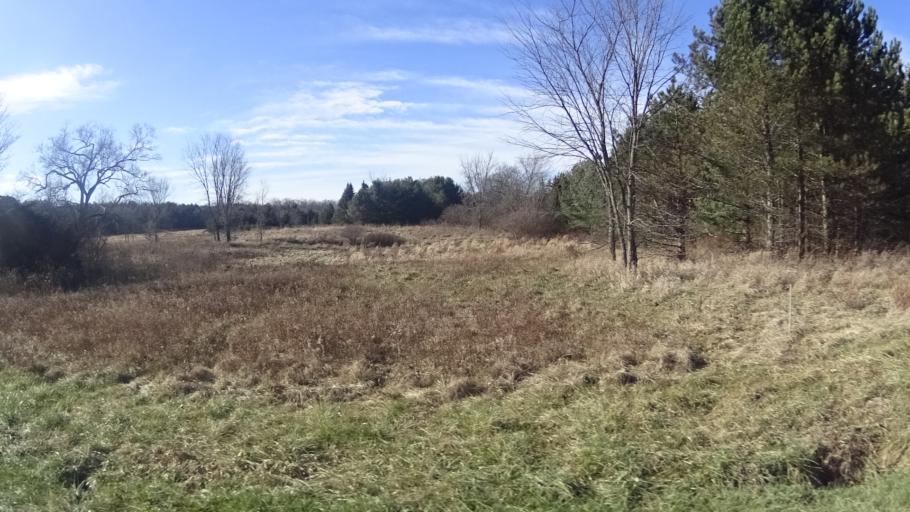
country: US
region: Ohio
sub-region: Lorain County
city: Camden
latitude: 41.2938
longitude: -82.3296
